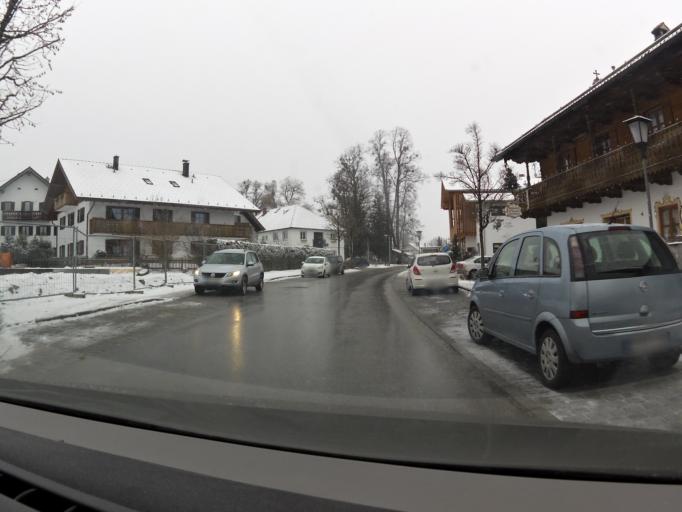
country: DE
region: Bavaria
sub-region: Upper Bavaria
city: Bichl
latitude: 47.7196
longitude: 11.4127
